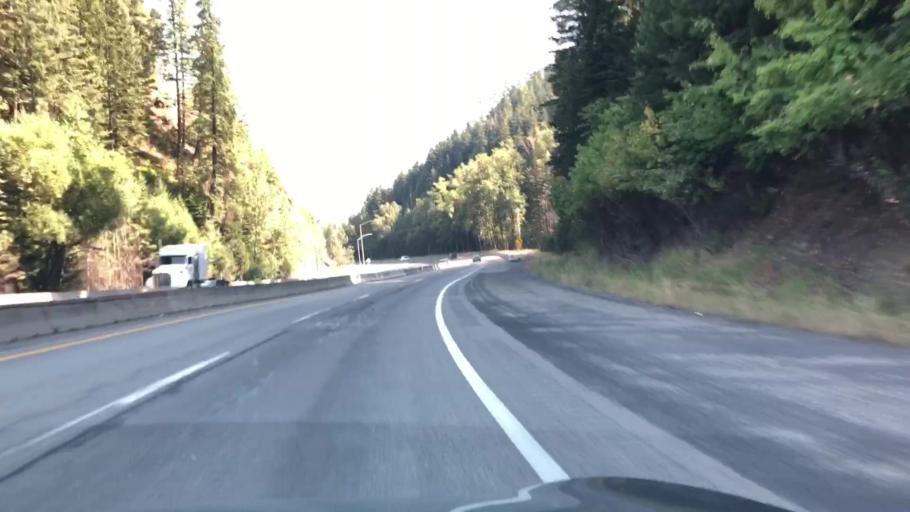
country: US
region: Idaho
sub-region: Shoshone County
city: Pinehurst
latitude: 47.5902
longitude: -116.4827
